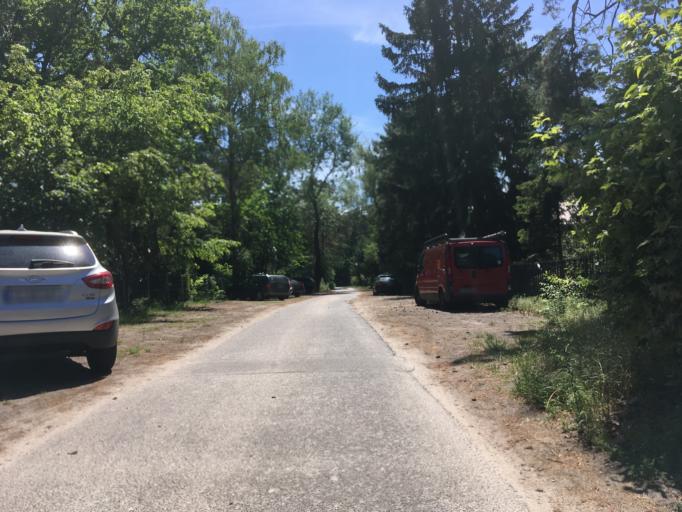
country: DE
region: Berlin
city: Schmockwitz
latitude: 52.3874
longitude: 13.6396
